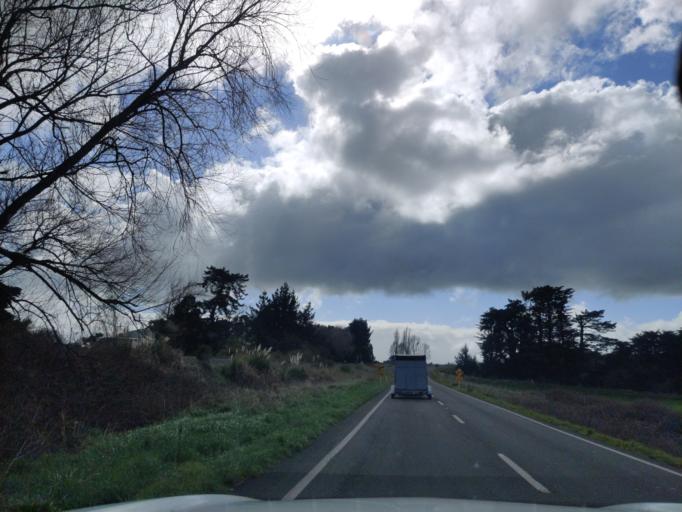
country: NZ
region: Manawatu-Wanganui
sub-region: Palmerston North City
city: Palmerston North
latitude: -40.4569
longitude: 175.5178
